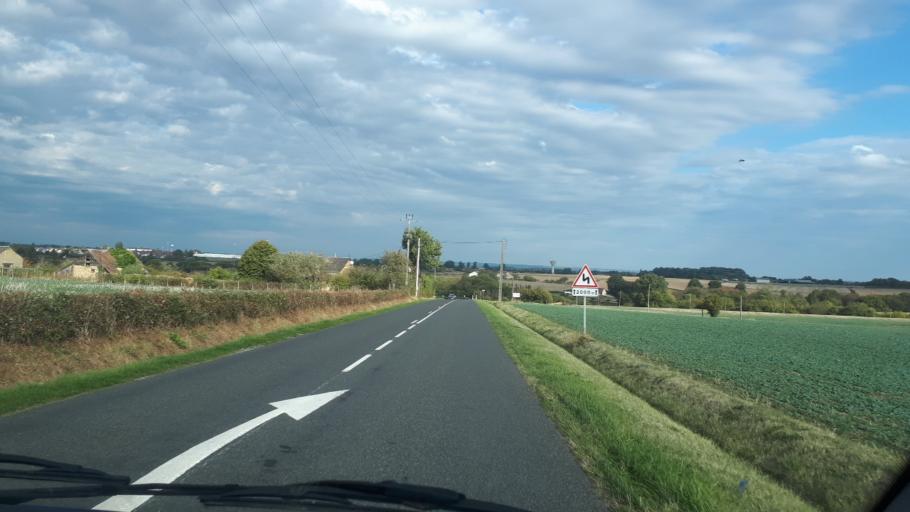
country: FR
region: Centre
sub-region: Departement du Loir-et-Cher
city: Mondoubleau
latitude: 47.9699
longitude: 0.9237
